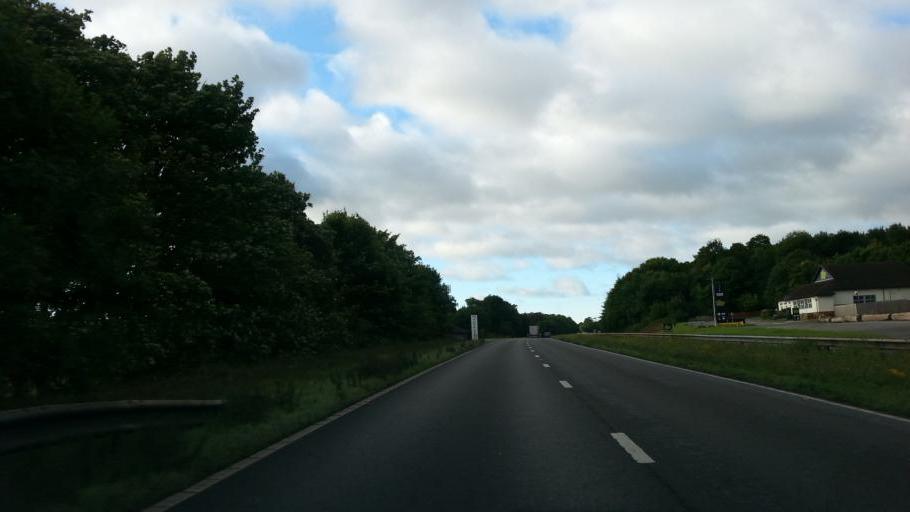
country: GB
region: England
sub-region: Lincolnshire
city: Grantham
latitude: 52.8391
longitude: -0.6288
